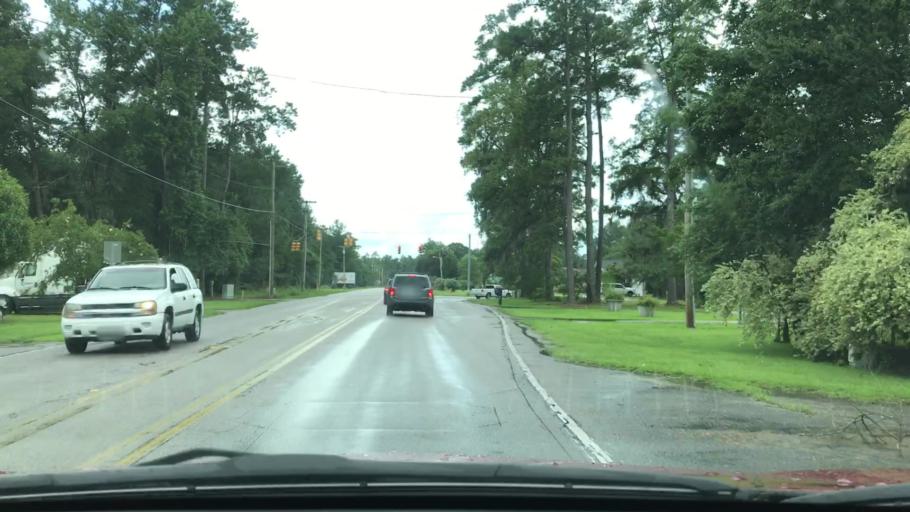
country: US
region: South Carolina
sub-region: Horry County
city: Conway
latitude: 33.8460
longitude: -79.0253
